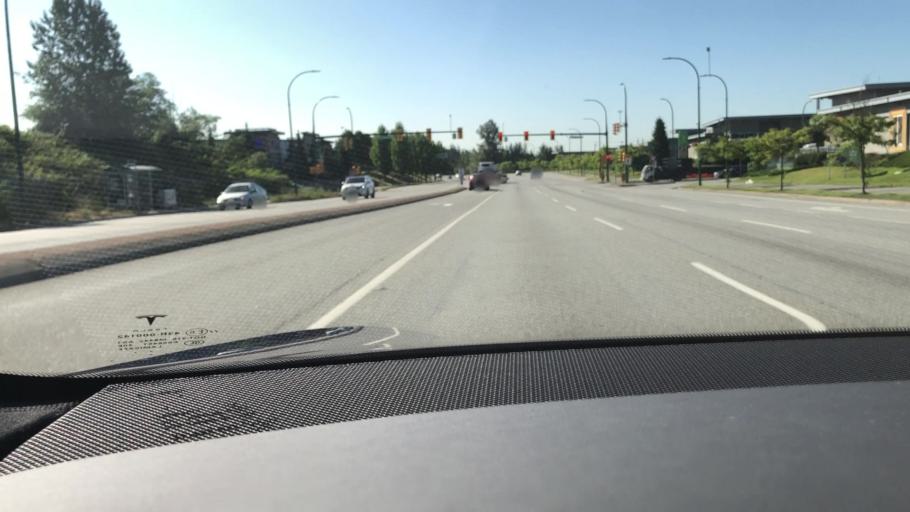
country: CA
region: British Columbia
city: New Westminster
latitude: 49.2004
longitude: -122.9800
